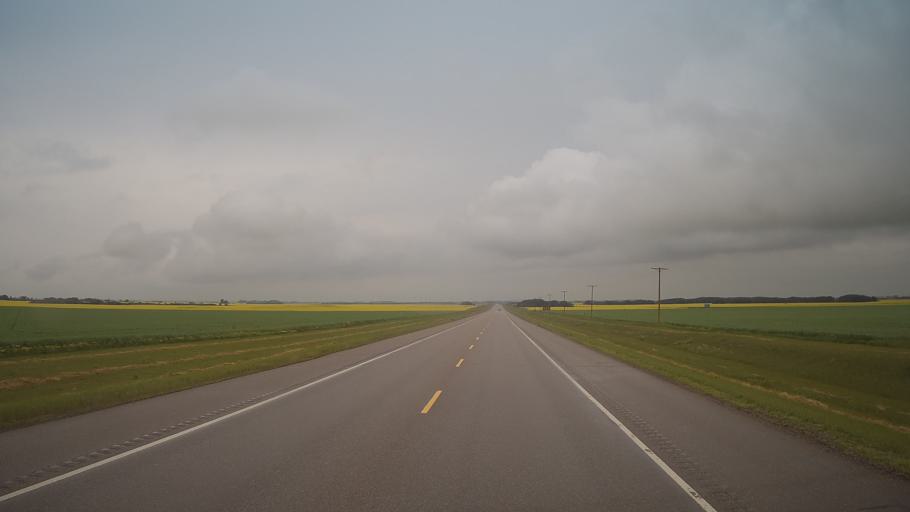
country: CA
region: Saskatchewan
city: Wilkie
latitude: 52.4216
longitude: -108.8981
